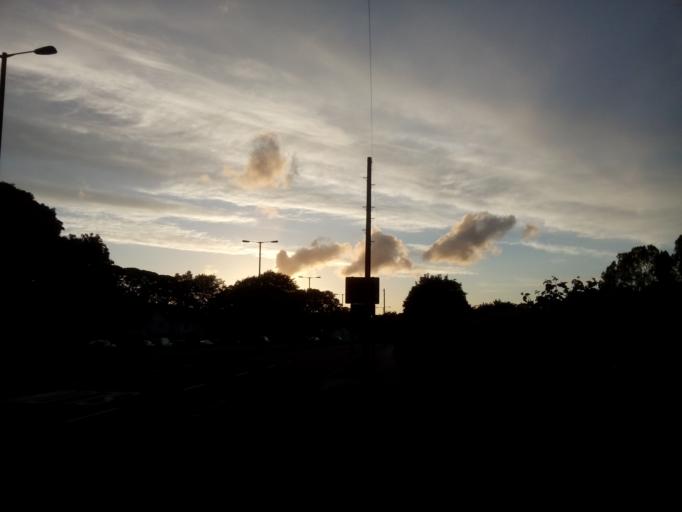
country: GB
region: England
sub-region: County Durham
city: Durham
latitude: 54.7826
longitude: -1.5838
